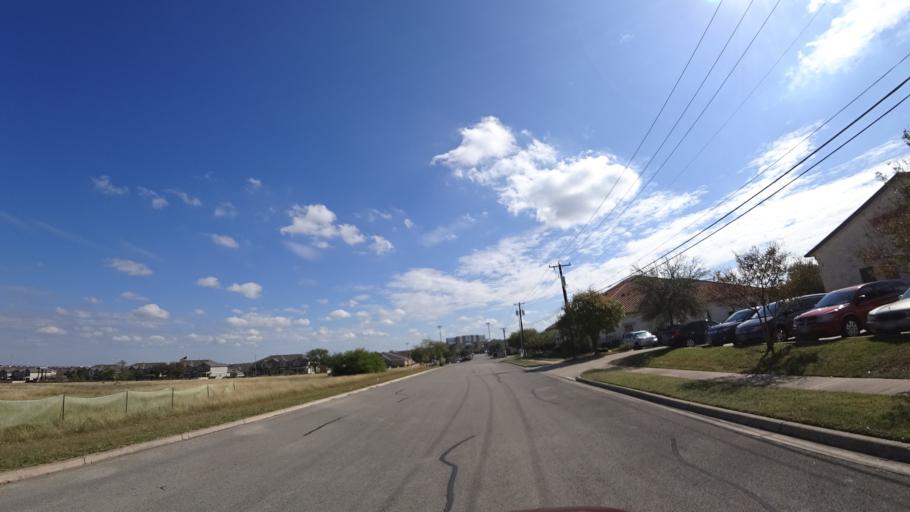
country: US
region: Texas
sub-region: Travis County
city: Windemere
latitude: 30.4505
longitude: -97.6396
